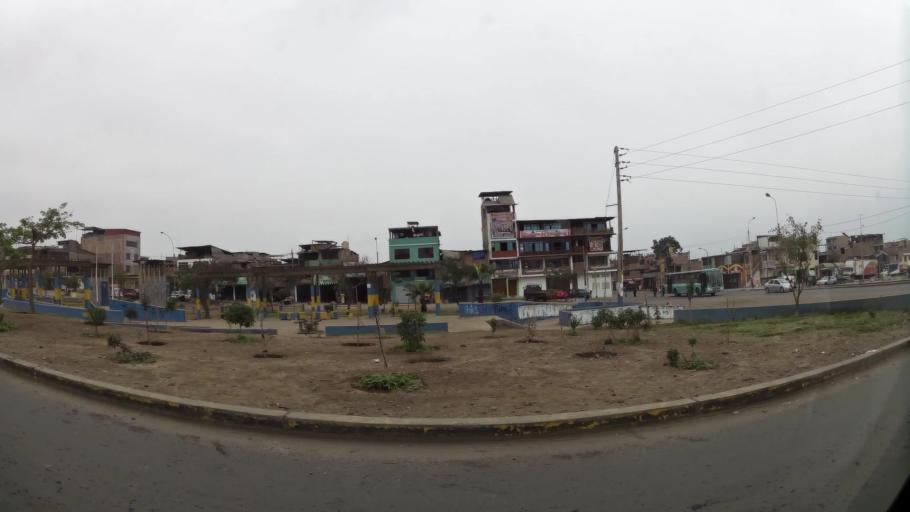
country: PE
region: Lima
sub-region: Lima
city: Surco
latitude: -12.2205
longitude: -76.9320
